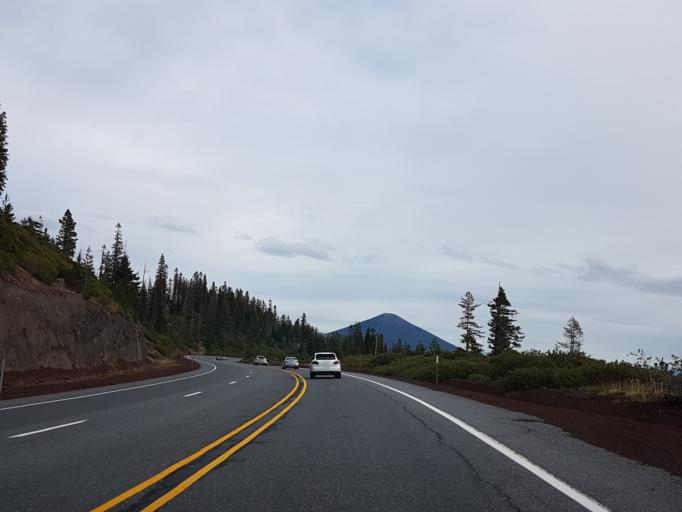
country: US
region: Oregon
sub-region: Deschutes County
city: Sisters
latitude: 44.4245
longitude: -121.8159
